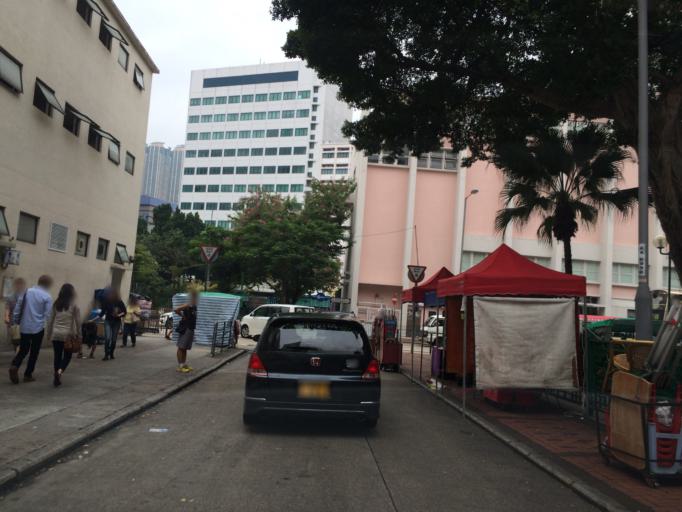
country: HK
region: Kowloon City
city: Kowloon
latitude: 22.3096
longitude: 114.1704
